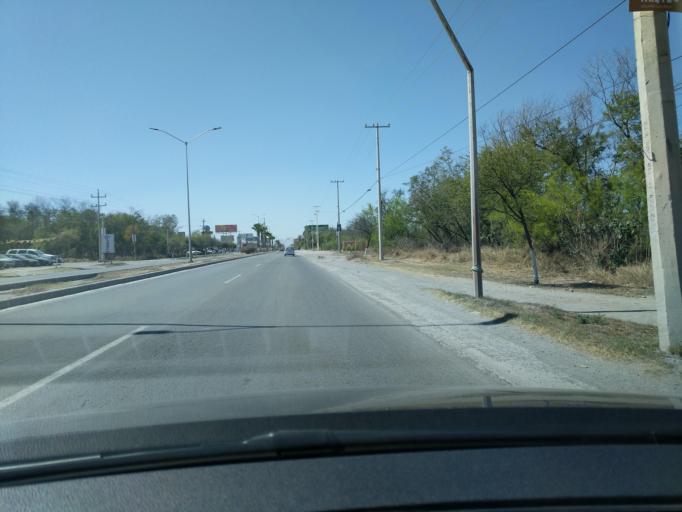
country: MX
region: Nuevo Leon
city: Juarez
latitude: 25.6364
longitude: -100.0830
